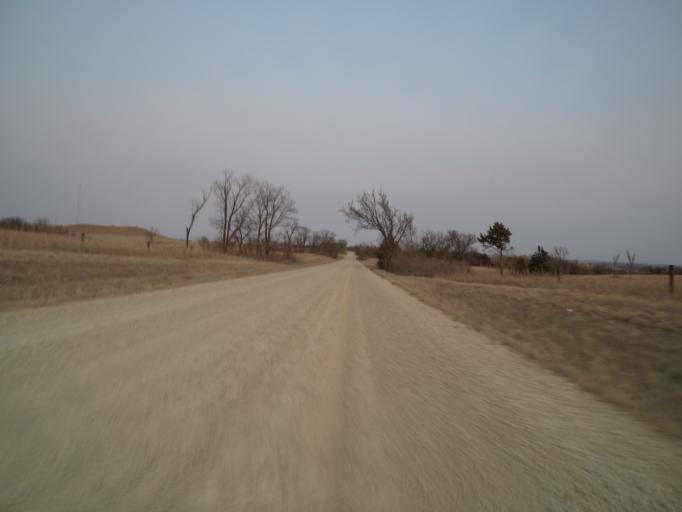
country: US
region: Kansas
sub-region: Riley County
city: Manhattan
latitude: 39.2237
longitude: -96.6245
